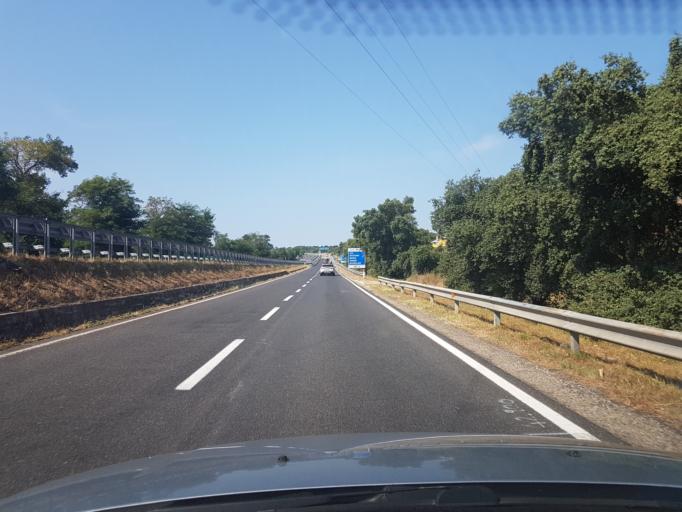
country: IT
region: Sardinia
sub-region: Provincia di Nuoro
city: Oniferi
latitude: 40.3083
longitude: 9.1977
